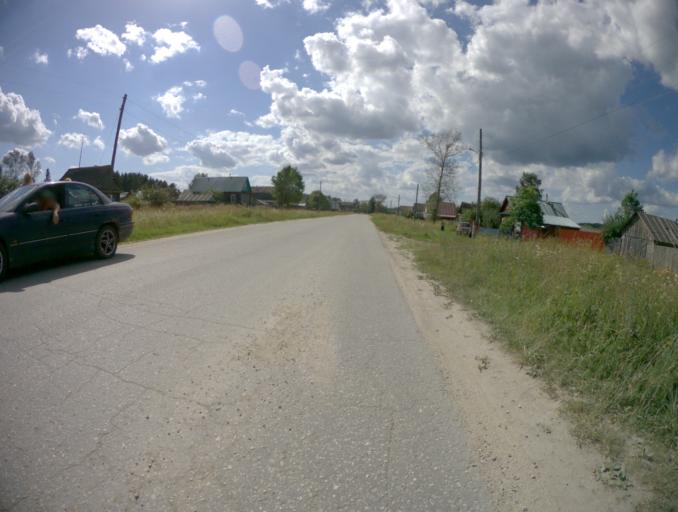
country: RU
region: Vladimir
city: Krasnyy Bogatyr'
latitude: 55.9772
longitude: 41.1285
